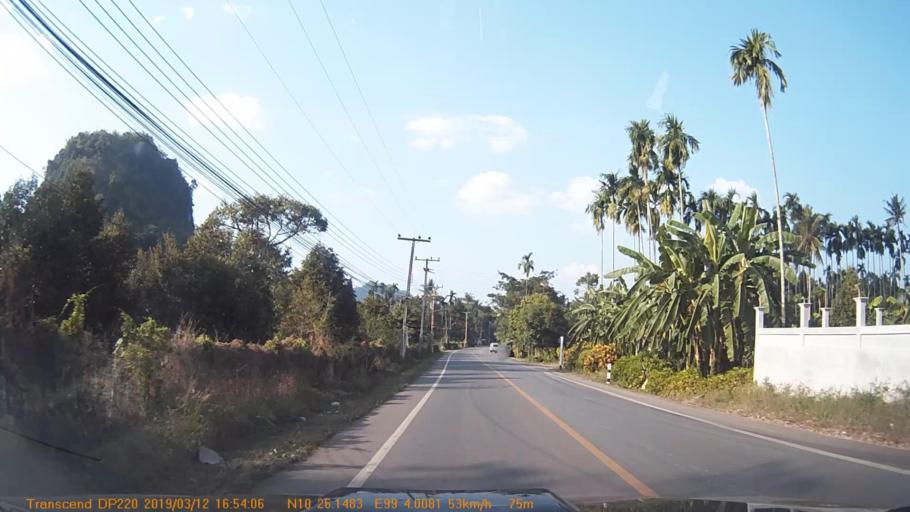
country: TH
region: Chumphon
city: Chumphon
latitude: 10.4363
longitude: 99.0670
